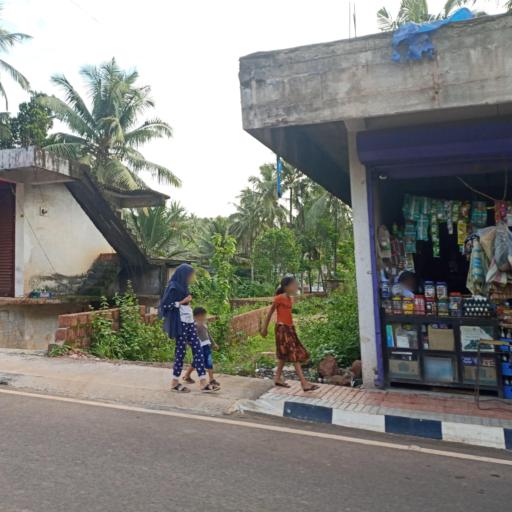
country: IN
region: Kerala
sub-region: Kasaragod District
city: Kasaragod
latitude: 12.5068
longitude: 75.0970
